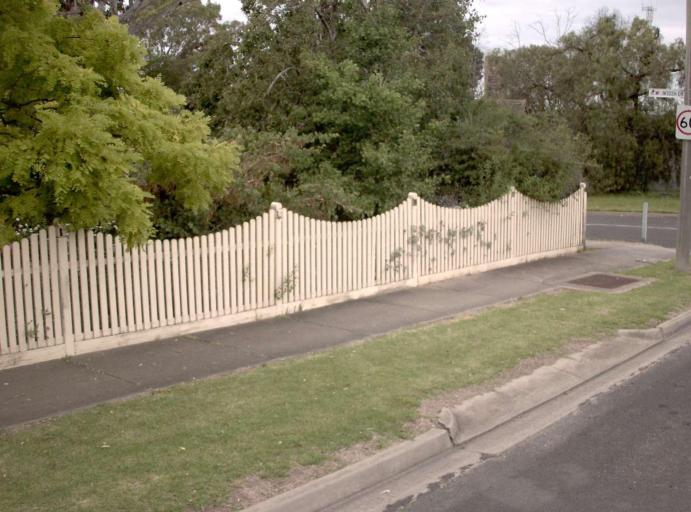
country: AU
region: Victoria
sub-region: Wellington
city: Sale
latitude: -38.1131
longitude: 147.0686
